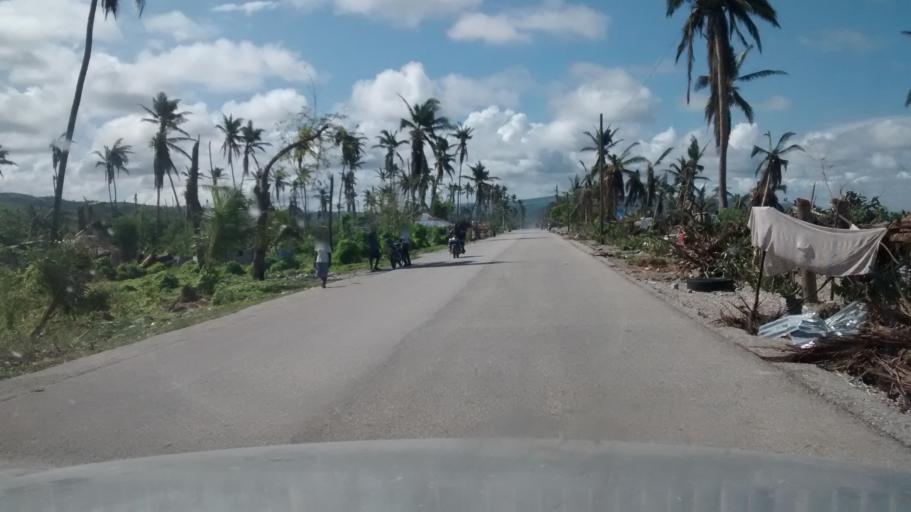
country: HT
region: Grandans
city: Jeremie
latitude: 18.6035
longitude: -74.0376
